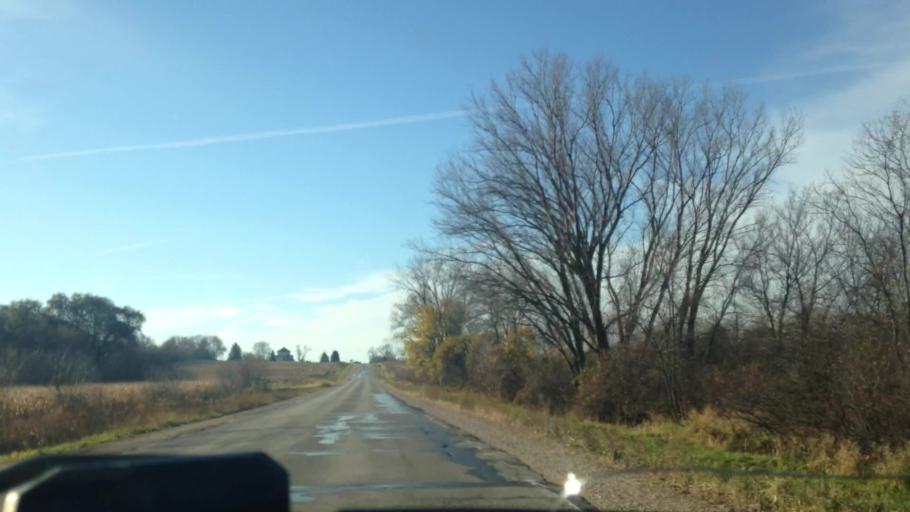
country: US
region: Wisconsin
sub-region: Dodge County
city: Mayville
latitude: 43.4487
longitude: -88.5000
